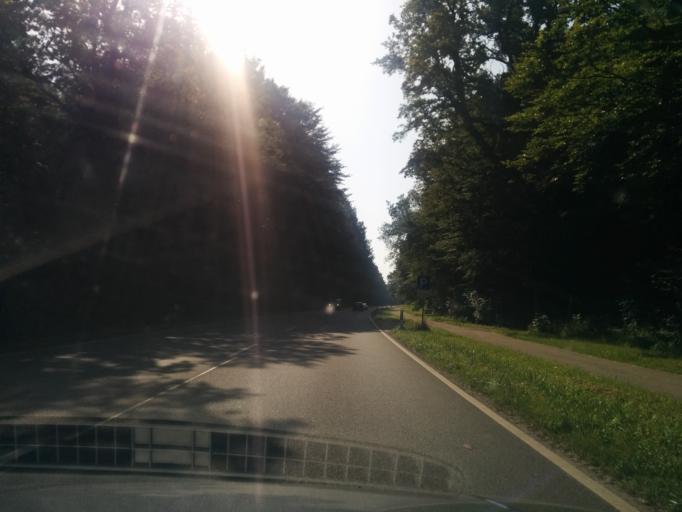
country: DE
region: Bavaria
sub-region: Upper Bavaria
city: Grunwald
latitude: 48.0362
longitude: 11.5419
